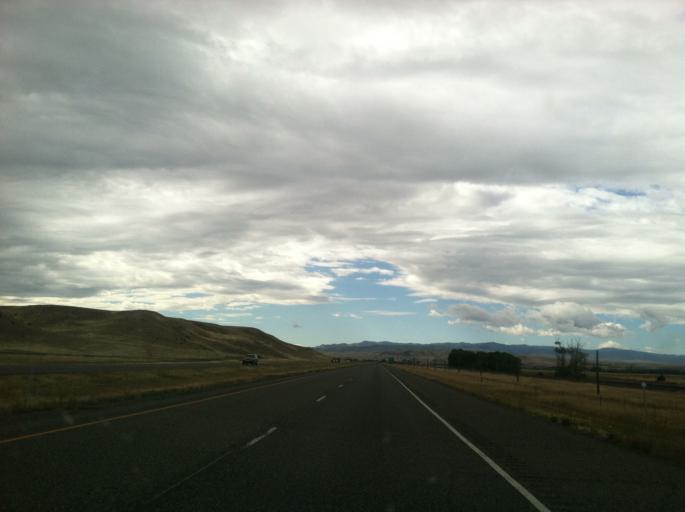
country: US
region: Montana
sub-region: Park County
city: Livingston
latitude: 45.7132
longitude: -110.4245
